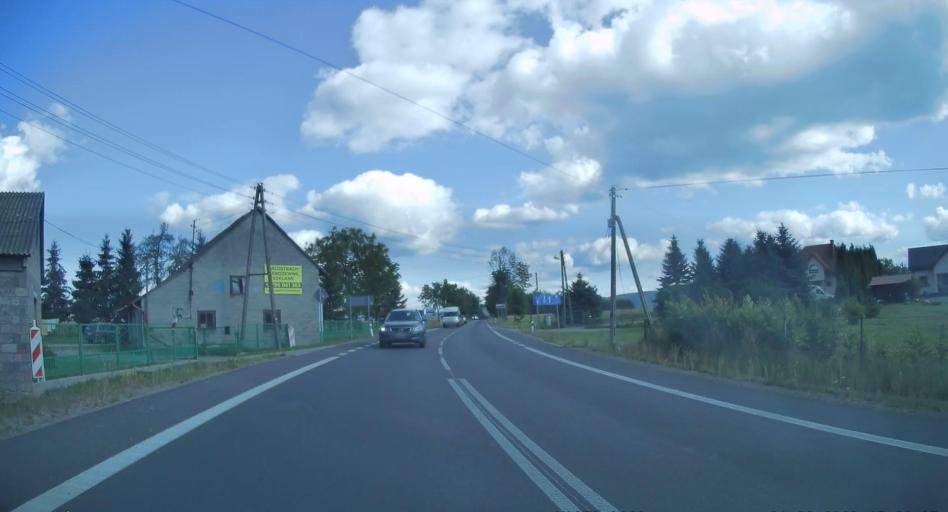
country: PL
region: Swietokrzyskie
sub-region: Powiat kielecki
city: Bodzentyn
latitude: 50.9306
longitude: 20.9789
